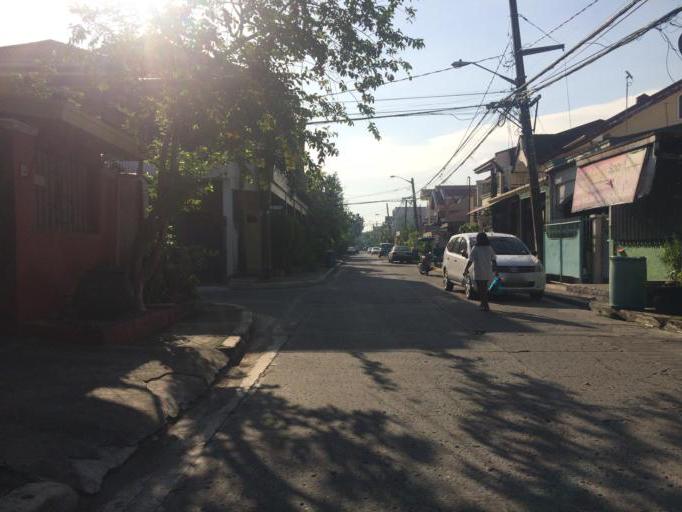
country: PH
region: Calabarzon
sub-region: Province of Rizal
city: Taytay
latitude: 14.5551
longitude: 121.1076
